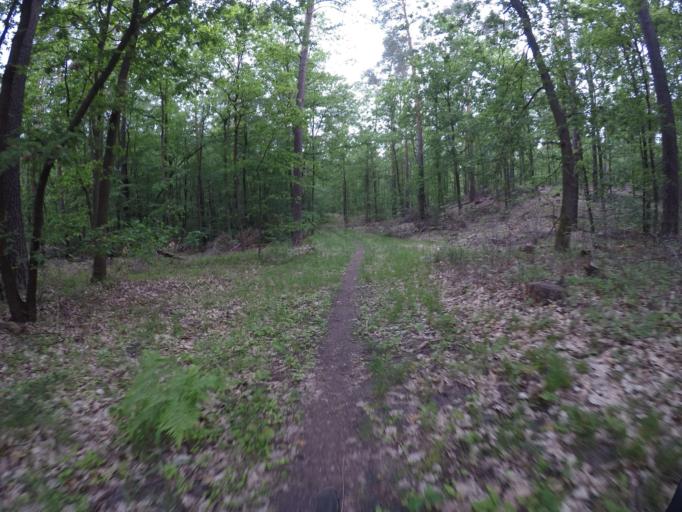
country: DE
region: Berlin
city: Heiligensee
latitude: 52.6227
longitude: 13.2613
